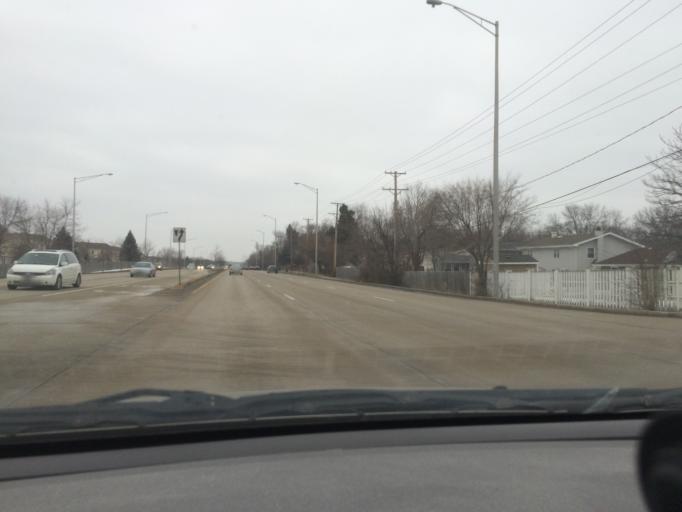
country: US
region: Illinois
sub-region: Cook County
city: Schaumburg
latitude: 42.0480
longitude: -88.1102
